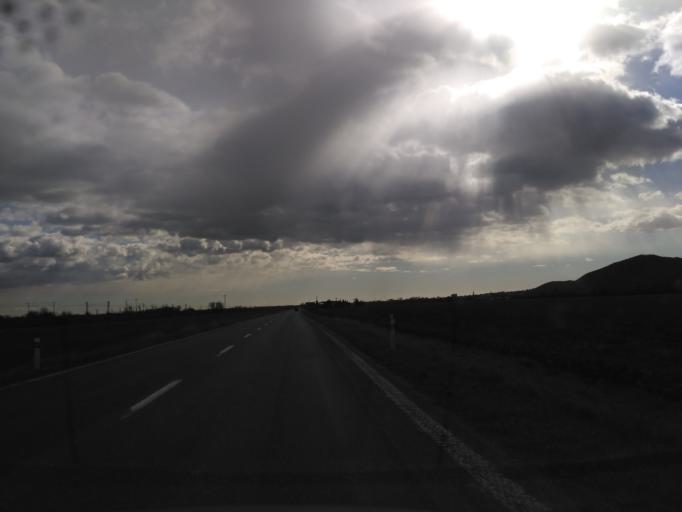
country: HU
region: Borsod-Abauj-Zemplen
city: Satoraljaujhely
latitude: 48.4337
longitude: 21.6576
